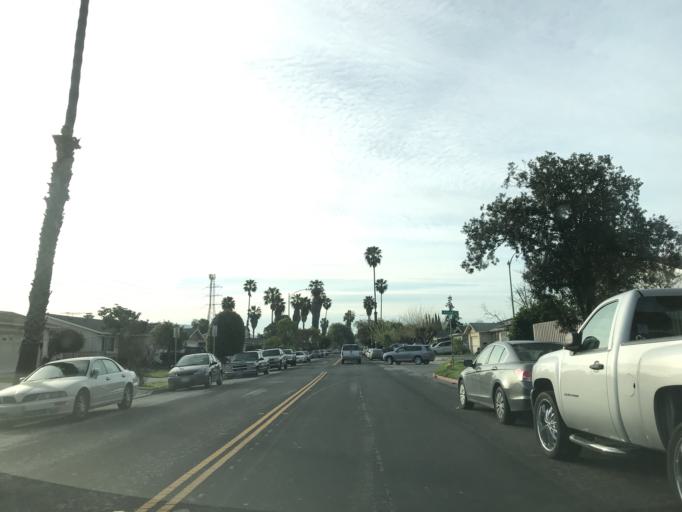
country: US
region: California
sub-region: Santa Clara County
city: Alum Rock
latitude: 37.3422
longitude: -121.8235
